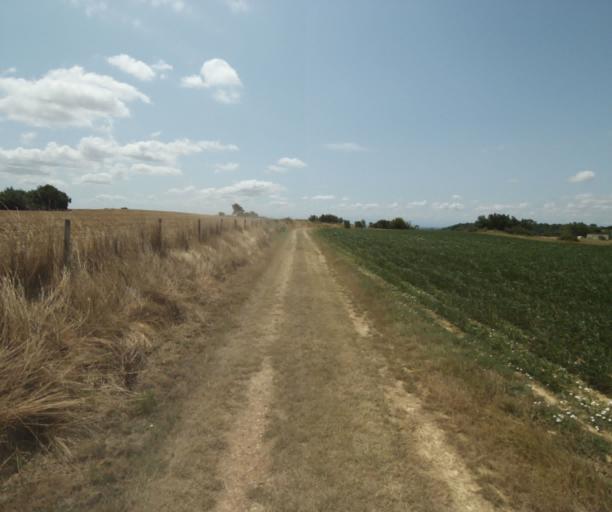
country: FR
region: Midi-Pyrenees
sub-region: Departement de la Haute-Garonne
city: Saint-Felix-Lauragais
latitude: 43.4420
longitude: 1.8931
